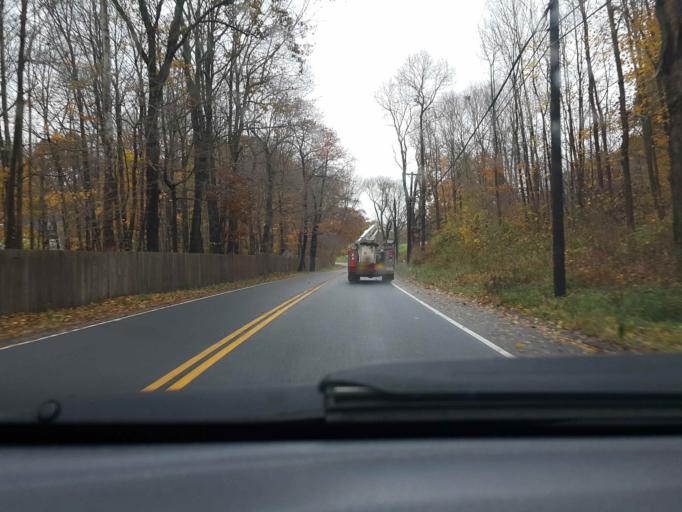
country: US
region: Connecticut
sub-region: Middlesex County
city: Durham
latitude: 41.4242
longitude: -72.6917
